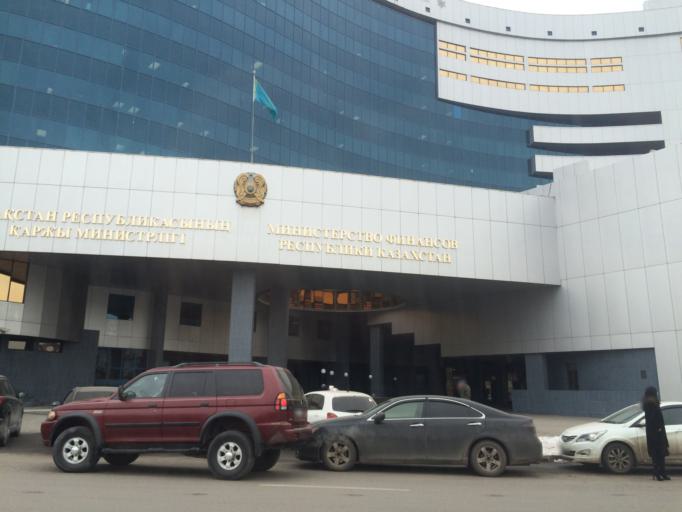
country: KZ
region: Astana Qalasy
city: Astana
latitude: 51.1661
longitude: 71.4140
